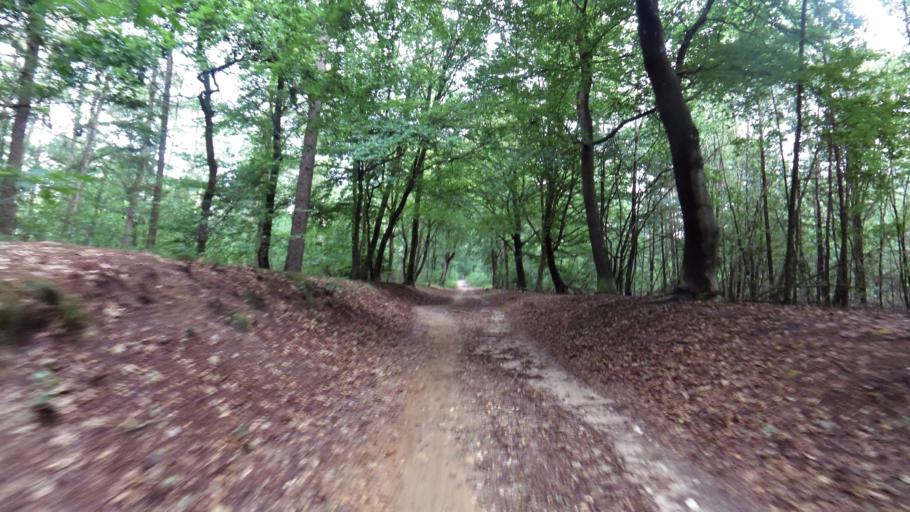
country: NL
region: Gelderland
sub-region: Gemeente Buren
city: Lienden
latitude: 51.9933
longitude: 5.5075
